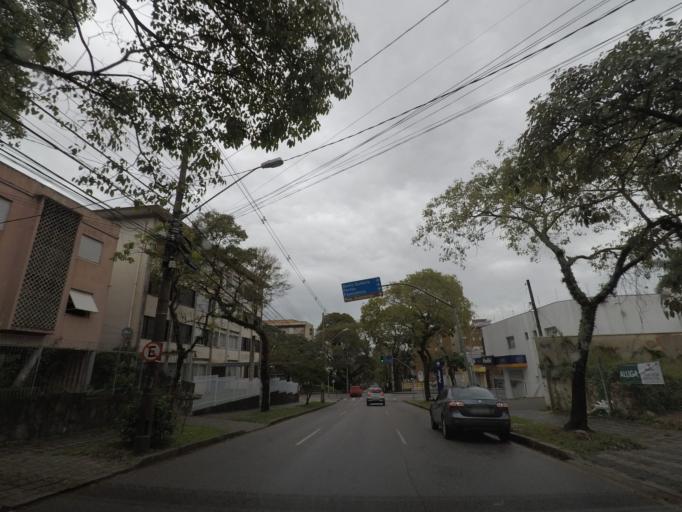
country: BR
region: Parana
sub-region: Curitiba
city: Curitiba
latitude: -25.4461
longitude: -49.2813
